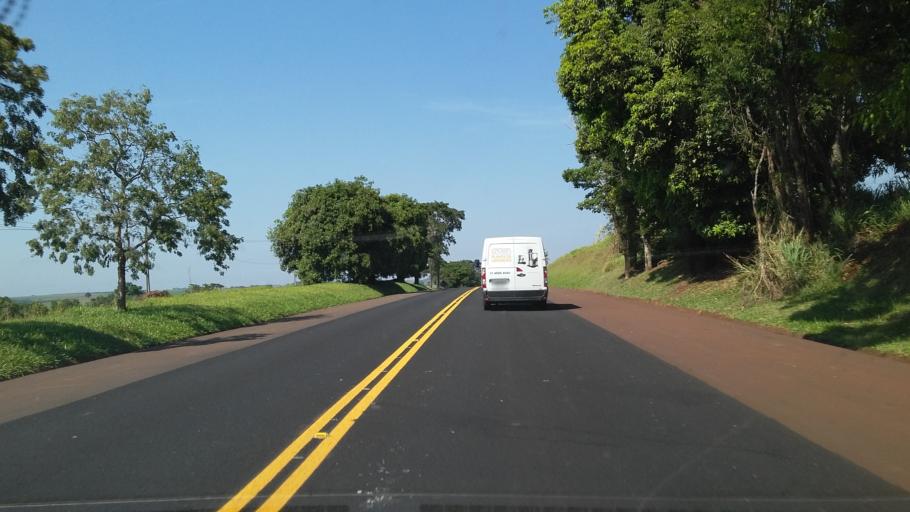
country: BR
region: Parana
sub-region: Bandeirantes
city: Bandeirantes
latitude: -23.1348
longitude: -50.4773
